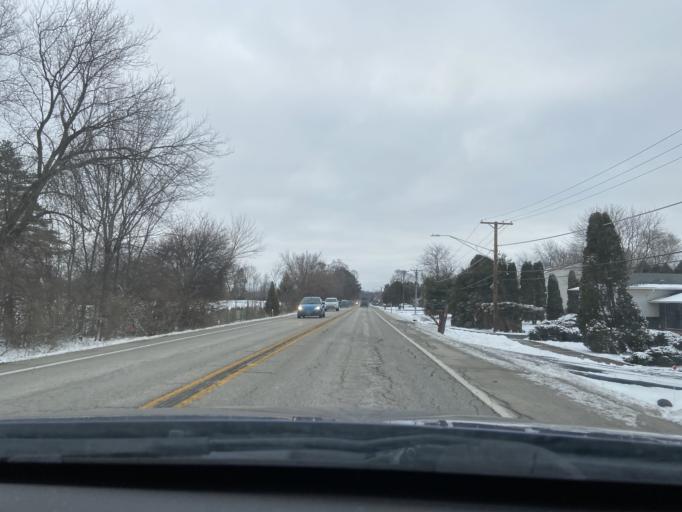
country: US
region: Illinois
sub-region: Lake County
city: Round Lake Park
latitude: 42.3765
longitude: -88.0646
